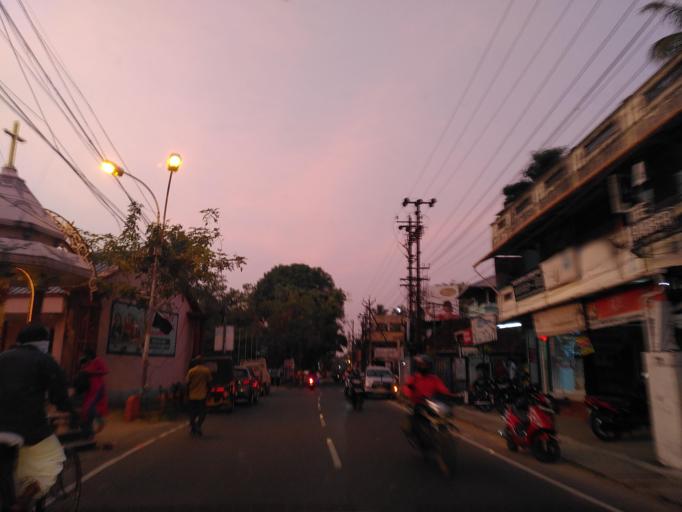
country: IN
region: Kerala
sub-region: Ernakulam
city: Cochin
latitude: 9.9088
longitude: 76.2802
